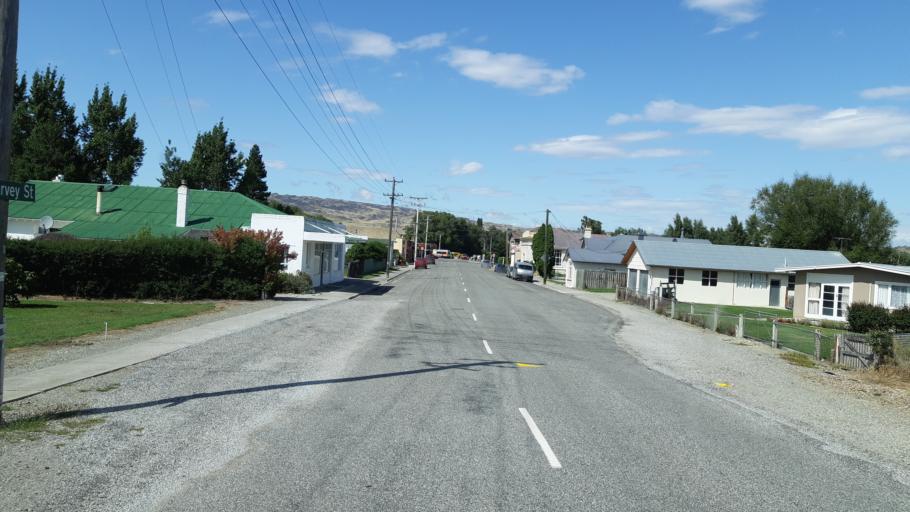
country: NZ
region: Otago
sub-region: Queenstown-Lakes District
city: Wanaka
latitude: -45.0923
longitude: 169.6019
